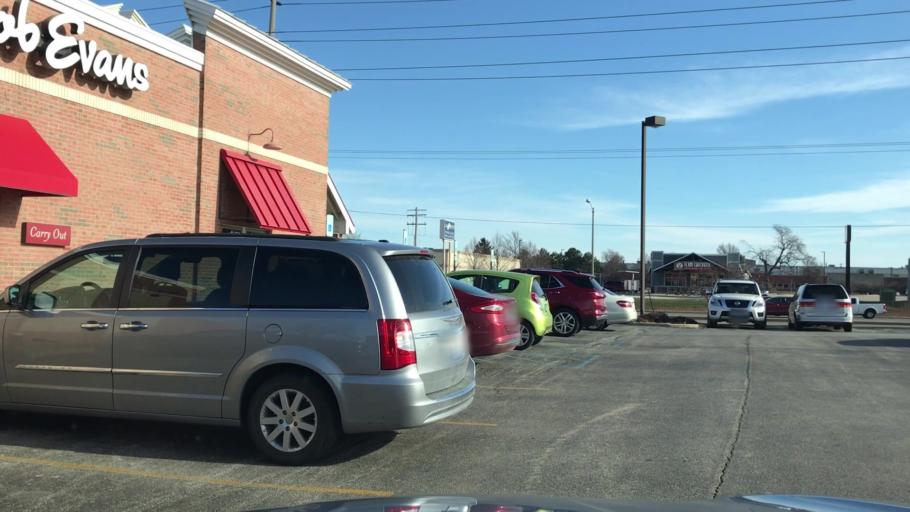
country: US
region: Illinois
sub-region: McLean County
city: Normal
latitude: 40.5011
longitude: -88.9539
